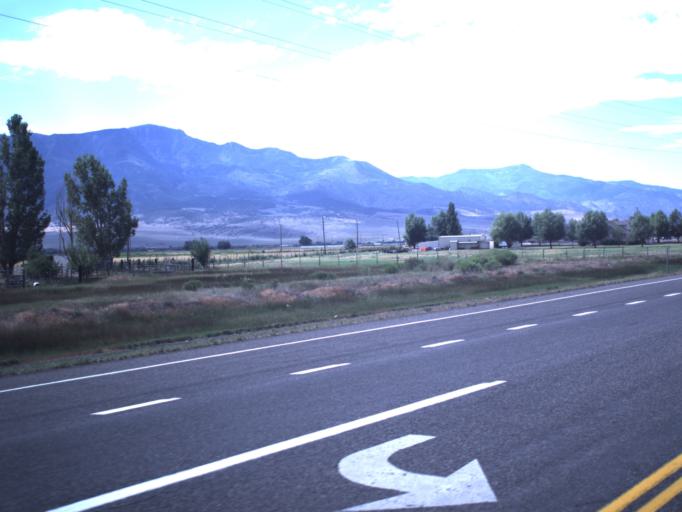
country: US
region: Utah
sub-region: Sevier County
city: Richfield
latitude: 38.7337
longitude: -112.0956
